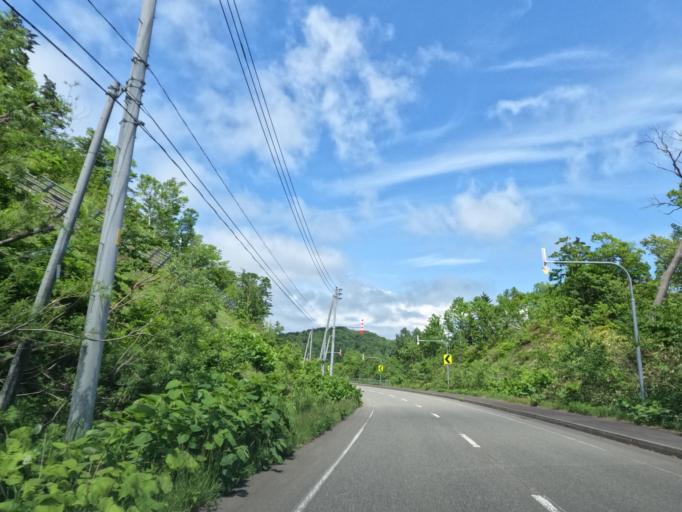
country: JP
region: Hokkaido
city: Tobetsu
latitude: 43.3275
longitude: 141.5721
